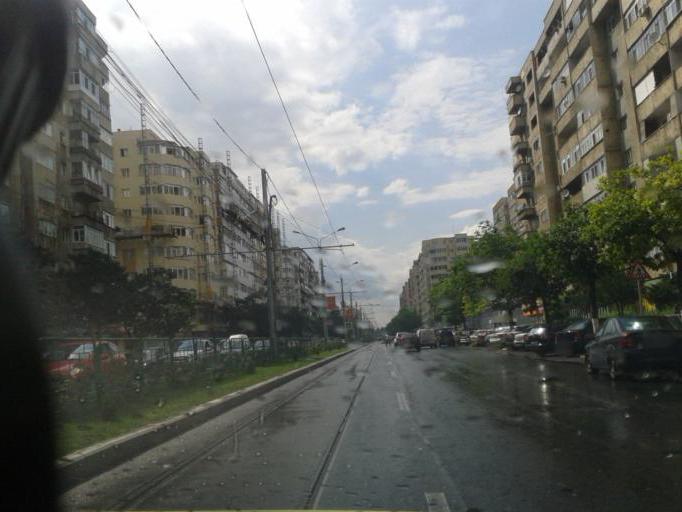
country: RO
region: Prahova
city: Ploiesti
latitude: 44.9486
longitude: 26.0078
